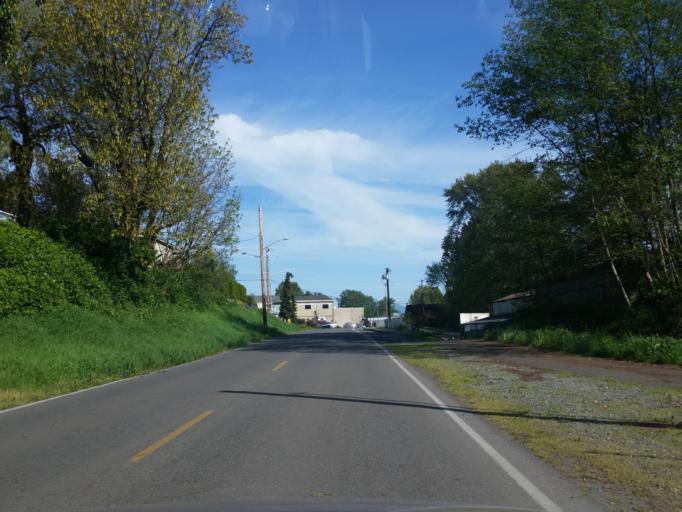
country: US
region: Washington
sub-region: Snohomish County
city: Snohomish
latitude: 47.9124
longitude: -122.1016
